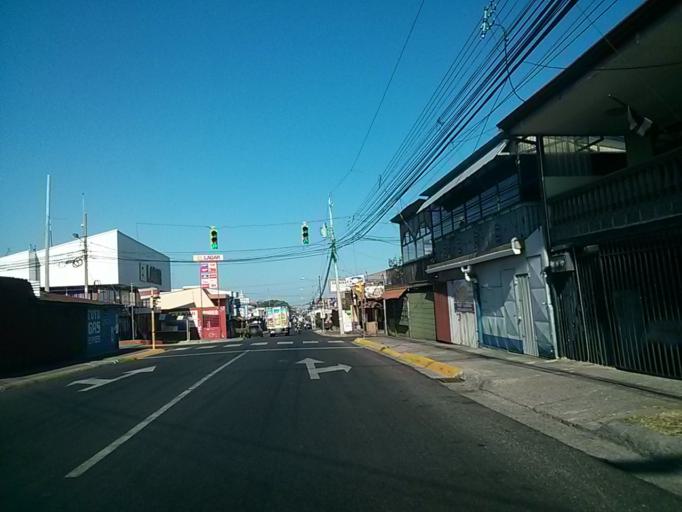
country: CR
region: Heredia
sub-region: Canton de Belen
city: San Antonio
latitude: 9.9801
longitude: -84.1820
